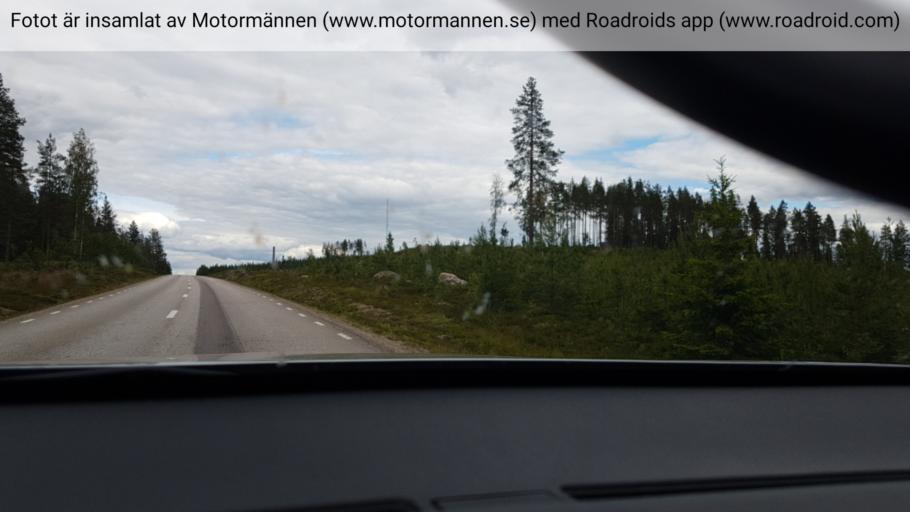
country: NO
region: Hedmark
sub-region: Trysil
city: Innbygda
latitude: 61.0249
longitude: 12.4945
